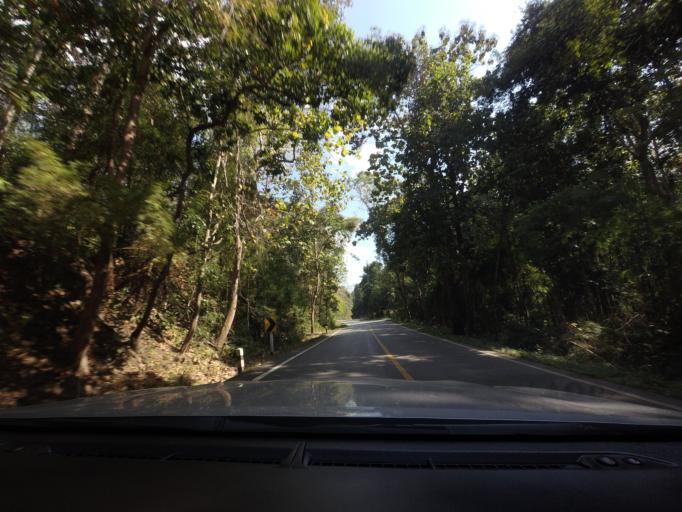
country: TH
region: Chiang Mai
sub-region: Amphoe Chiang Dao
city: Chiang Dao
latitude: 19.4789
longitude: 99.0104
